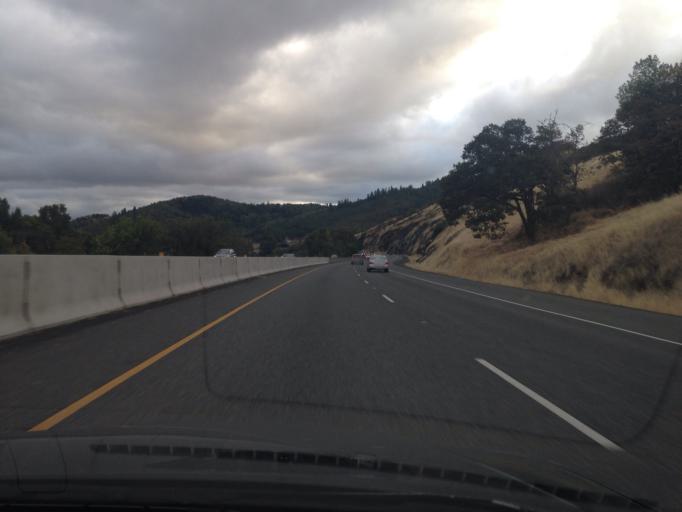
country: US
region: Oregon
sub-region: Douglas County
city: Green
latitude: 43.1920
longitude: -123.3642
